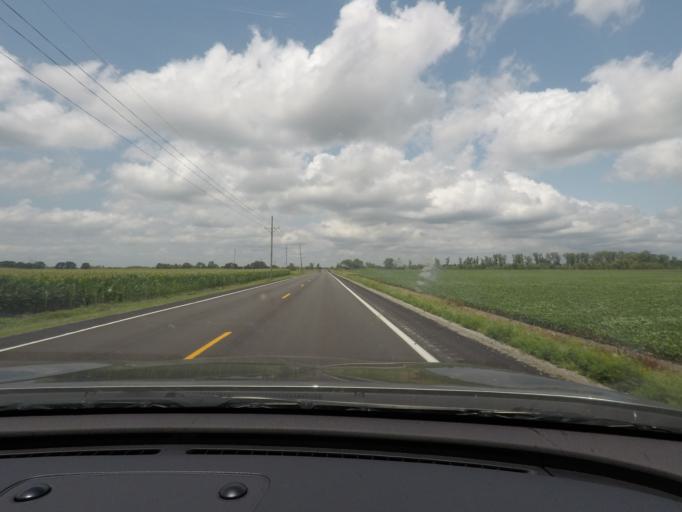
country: US
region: Missouri
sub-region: Carroll County
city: Carrollton
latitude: 39.2696
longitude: -93.5123
